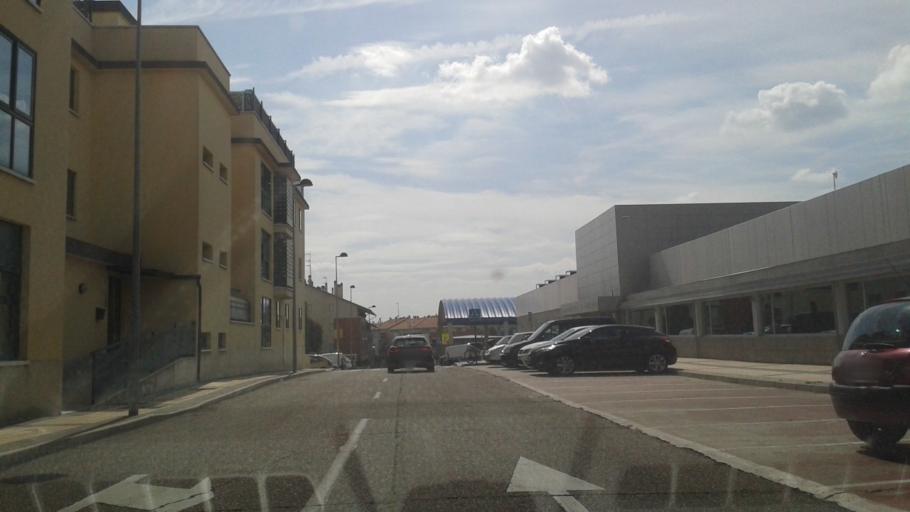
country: ES
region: Castille and Leon
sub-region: Provincia de Valladolid
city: Arroyo
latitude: 41.6280
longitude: -4.7759
